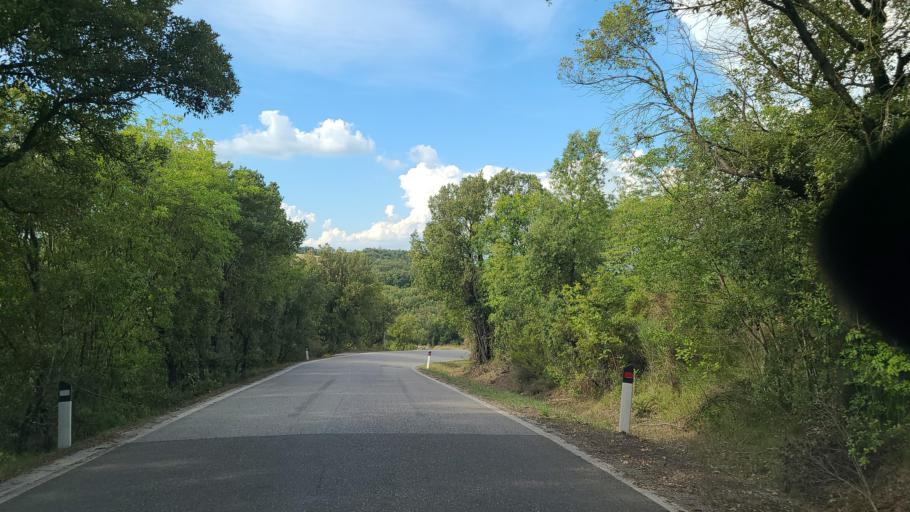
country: IT
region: Tuscany
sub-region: Provincia di Siena
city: San Gimignano
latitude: 43.4217
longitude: 10.9759
